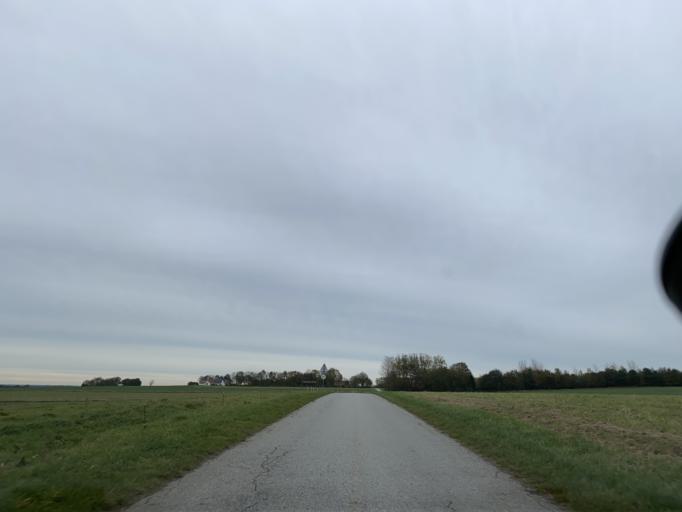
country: DK
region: Central Jutland
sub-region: Skanderborg Kommune
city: Ry
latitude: 56.1848
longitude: 9.7750
